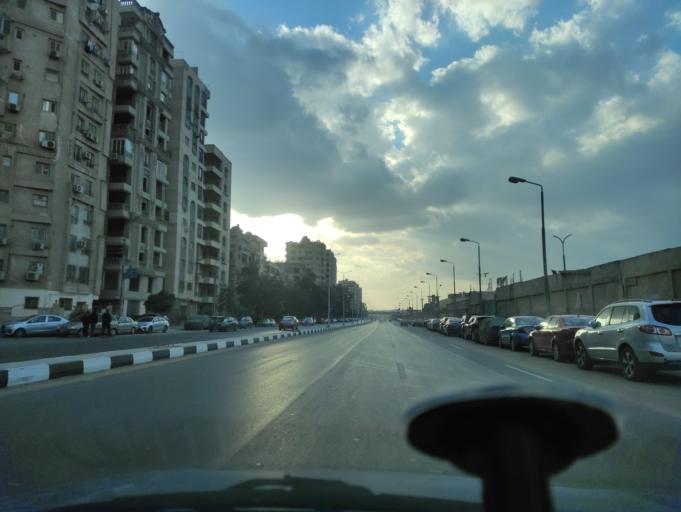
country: EG
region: Muhafazat al Qalyubiyah
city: Al Khankah
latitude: 30.1278
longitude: 31.3703
